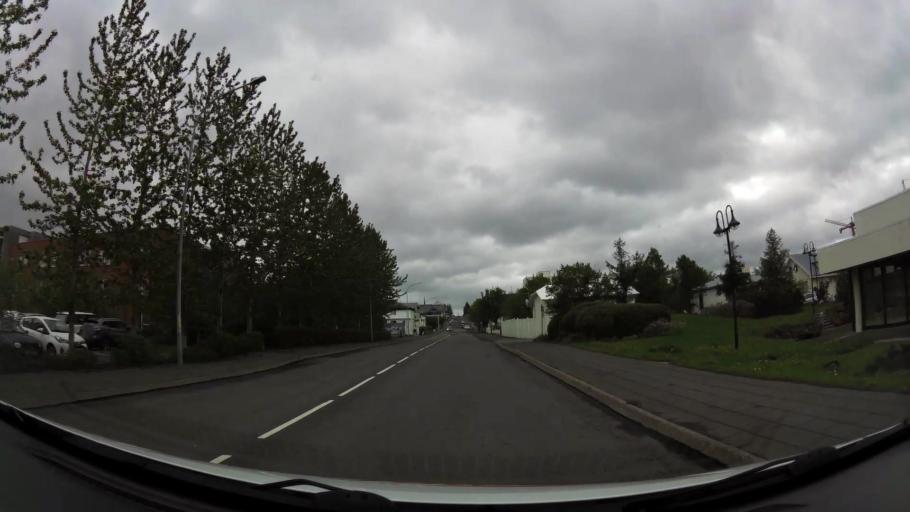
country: IS
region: Capital Region
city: Reykjavik
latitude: 64.1447
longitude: -21.9013
